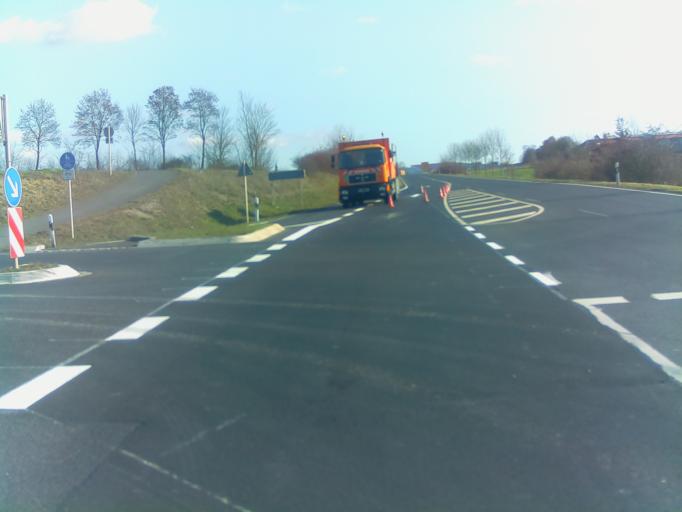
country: DE
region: Bavaria
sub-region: Regierungsbezirk Unterfranken
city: Bad Konigshofen im Grabfeld
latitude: 50.2992
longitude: 10.4446
